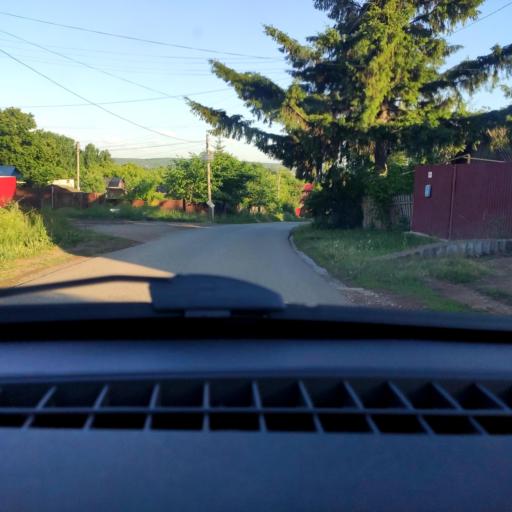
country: RU
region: Bashkortostan
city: Avdon
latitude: 54.6179
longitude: 55.6523
